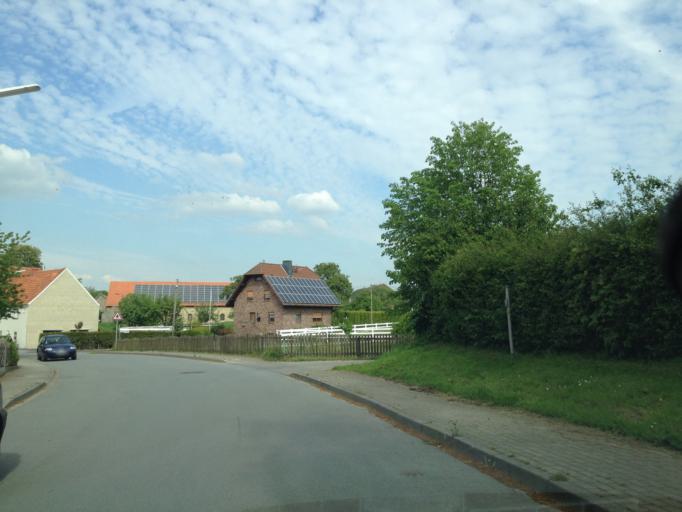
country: DE
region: North Rhine-Westphalia
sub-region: Regierungsbezirk Arnsberg
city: Welver
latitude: 51.5310
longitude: 8.0095
